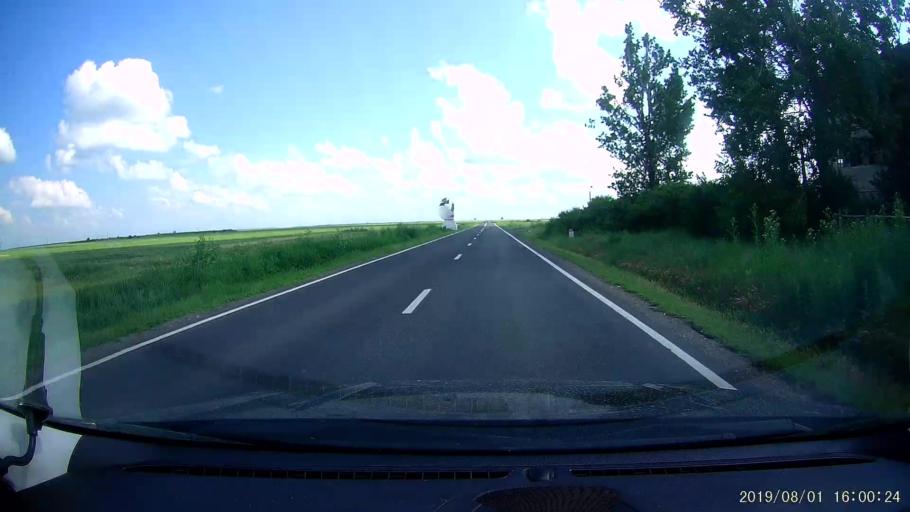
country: RO
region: Ialomita
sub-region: Comuna Ciulnita
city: Ciulnita
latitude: 44.5303
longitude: 27.3887
